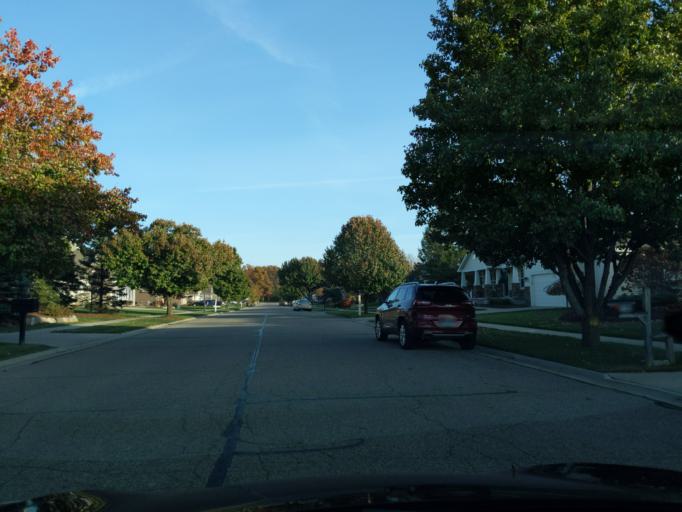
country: US
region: Michigan
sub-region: Clinton County
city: Bath
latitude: 42.8000
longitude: -84.4675
